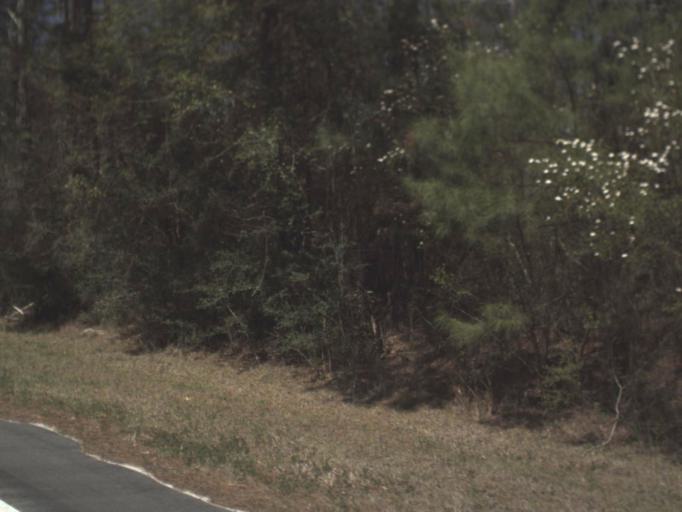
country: US
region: Florida
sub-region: Wakulla County
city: Crawfordville
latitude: 30.2575
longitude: -84.3504
